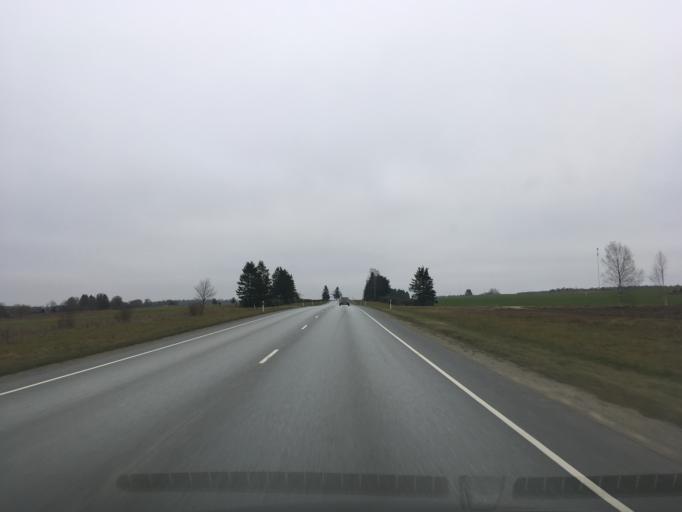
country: EE
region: Laeaene-Virumaa
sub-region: Viru-Nigula vald
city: Kunda
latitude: 59.4225
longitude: 26.6646
